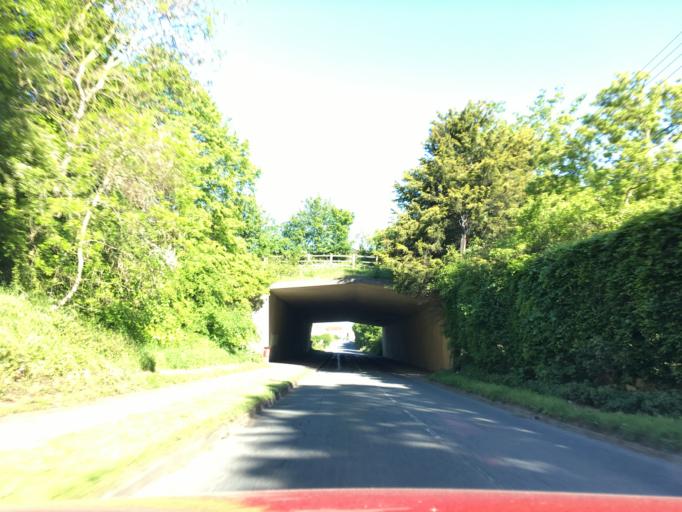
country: GB
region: England
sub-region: South Gloucestershire
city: Severn Beach
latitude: 51.5151
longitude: -2.6460
